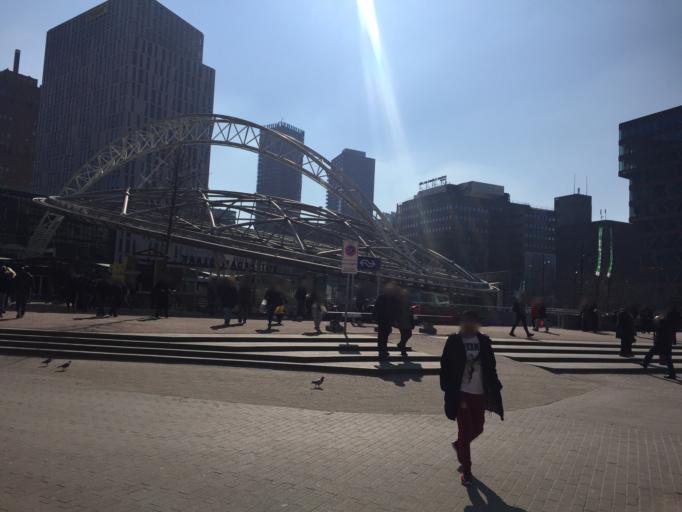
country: NL
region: South Holland
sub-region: Gemeente Rotterdam
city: Rotterdam
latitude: 51.9206
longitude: 4.4890
